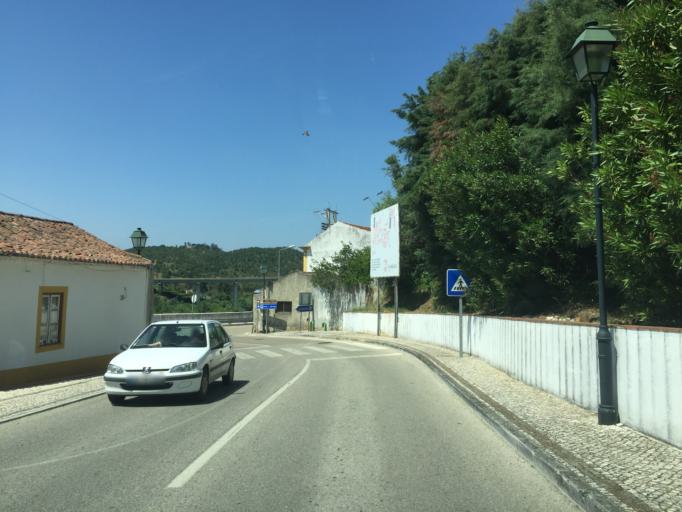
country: PT
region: Santarem
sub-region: Constancia
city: Constancia
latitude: 39.4773
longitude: -8.3407
